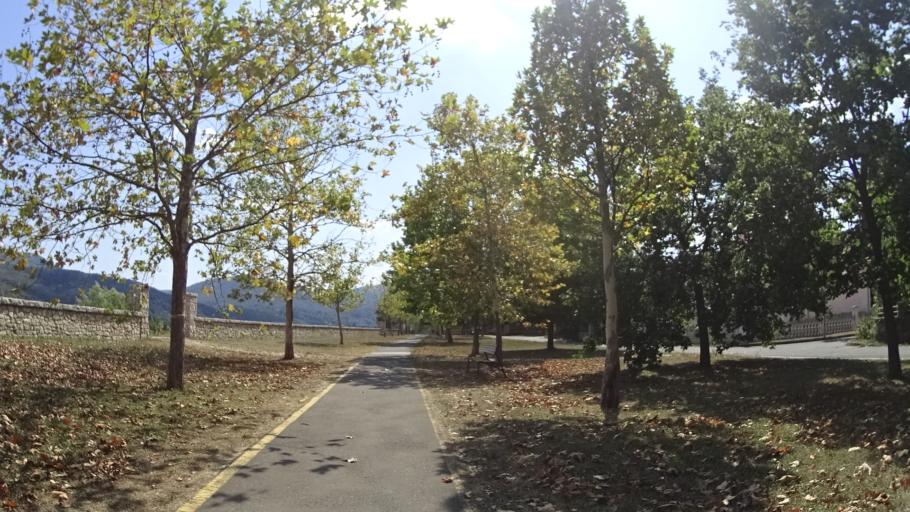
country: HU
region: Pest
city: Nagymaros
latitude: 47.7809
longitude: 18.9566
